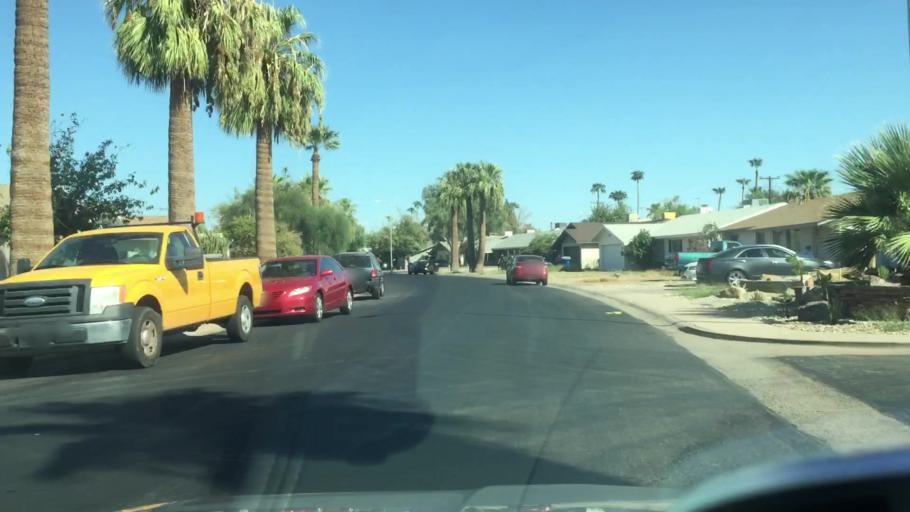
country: US
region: Arizona
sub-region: Maricopa County
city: Tempe Junction
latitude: 33.3952
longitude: -111.9376
